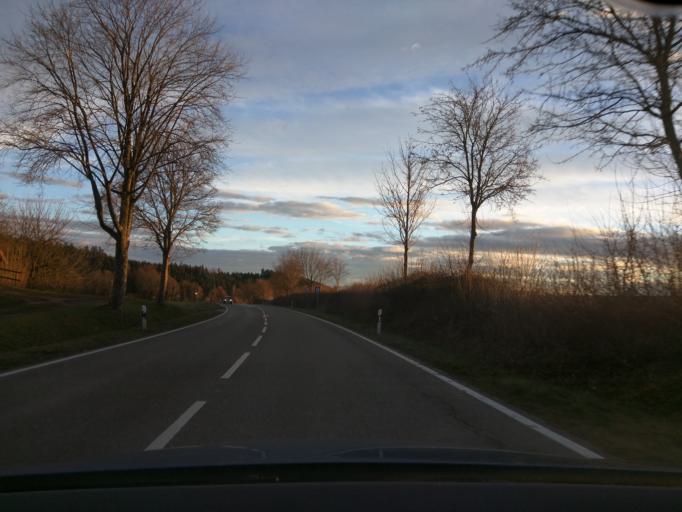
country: DE
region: Bavaria
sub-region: Upper Bavaria
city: Attenkirchen
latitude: 48.4908
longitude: 11.7620
